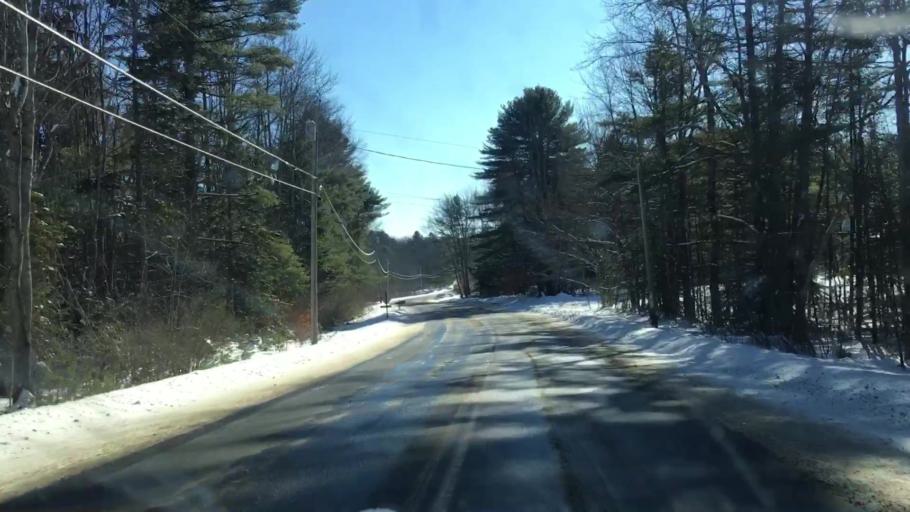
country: US
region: Maine
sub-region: Sagadahoc County
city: Topsham
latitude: 43.9250
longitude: -70.0455
